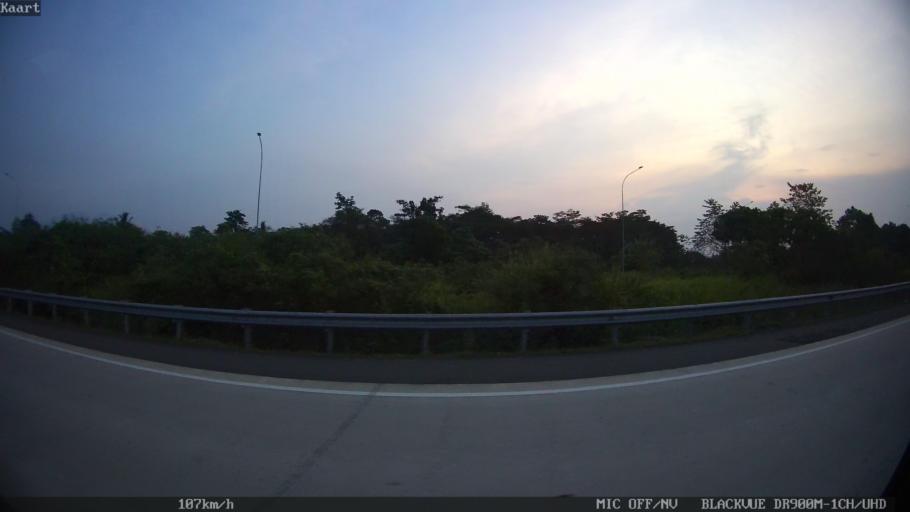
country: ID
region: Lampung
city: Kalianda
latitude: -5.6927
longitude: 105.6224
